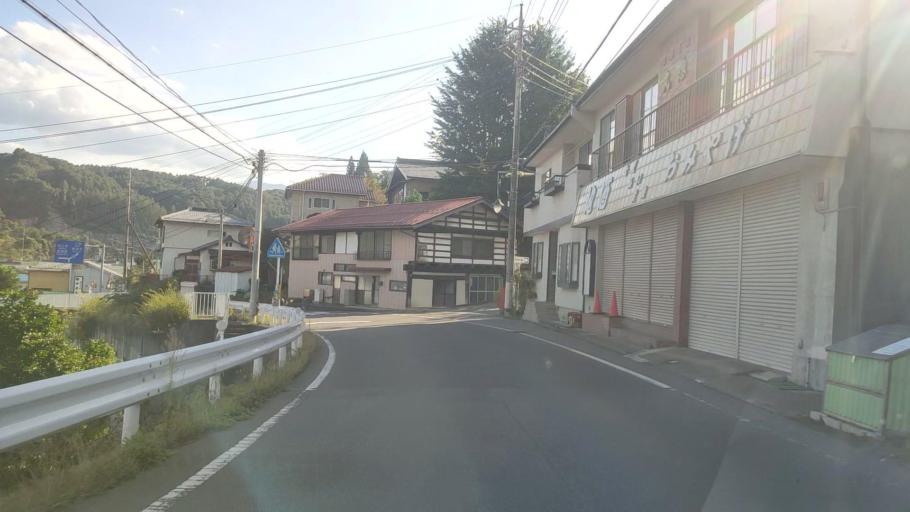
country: JP
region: Nagano
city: Komoro
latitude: 36.5355
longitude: 138.5493
